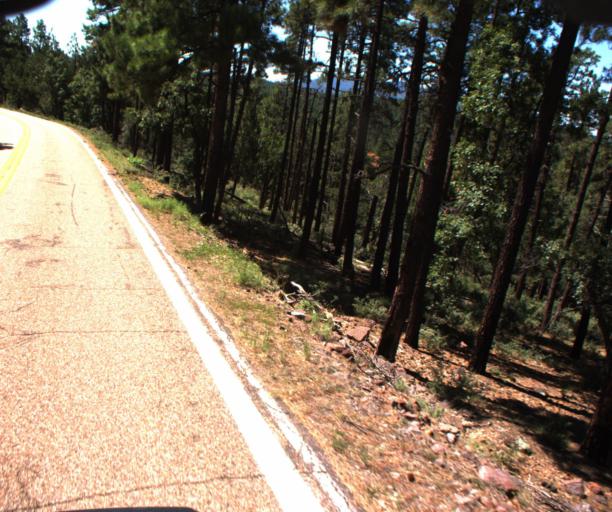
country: US
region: Arizona
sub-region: Greenlee County
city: Morenci
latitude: 33.5259
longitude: -109.3086
